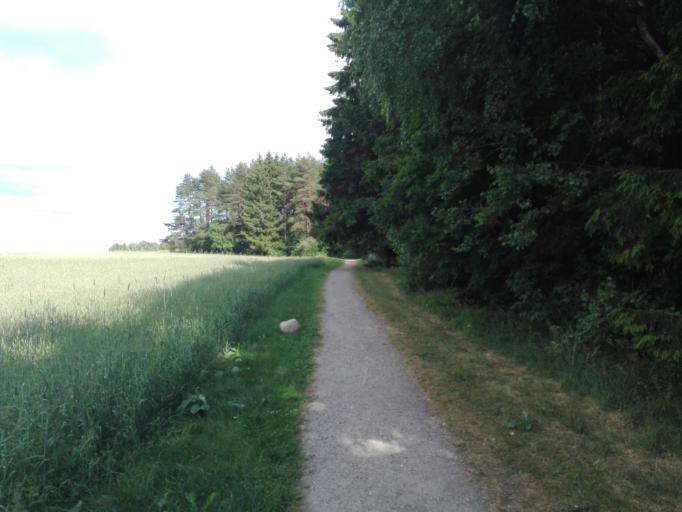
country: LT
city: Skaidiskes
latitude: 54.5270
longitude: 25.6228
